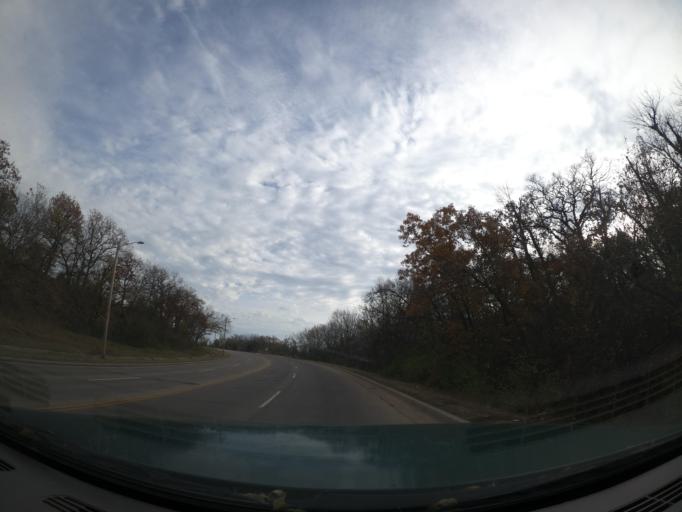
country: US
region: Oklahoma
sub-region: Tulsa County
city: Turley
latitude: 36.2124
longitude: -95.9963
